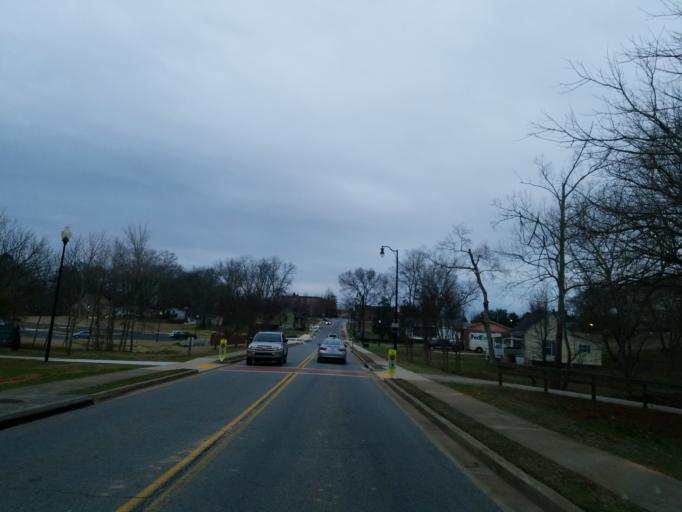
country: US
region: Georgia
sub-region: Cobb County
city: Acworth
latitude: 34.0696
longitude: -84.6769
